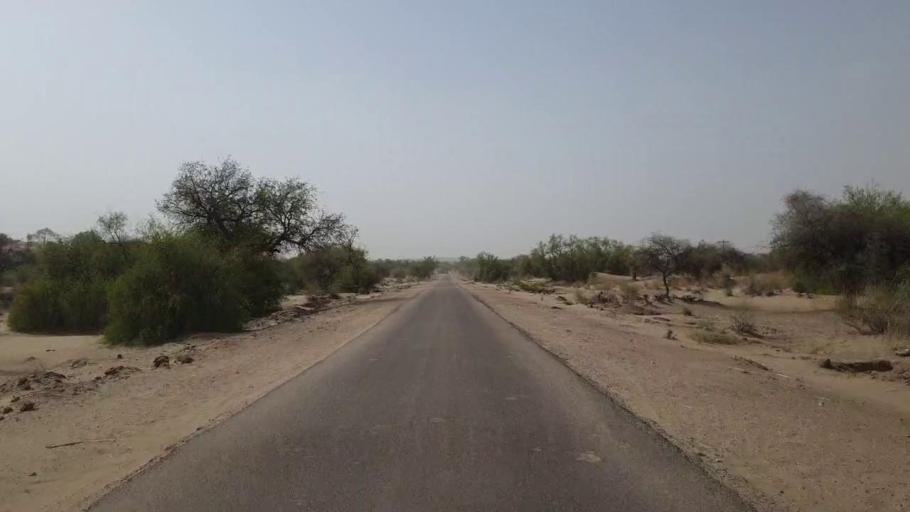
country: PK
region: Sindh
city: Mithi
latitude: 24.6059
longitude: 69.9216
